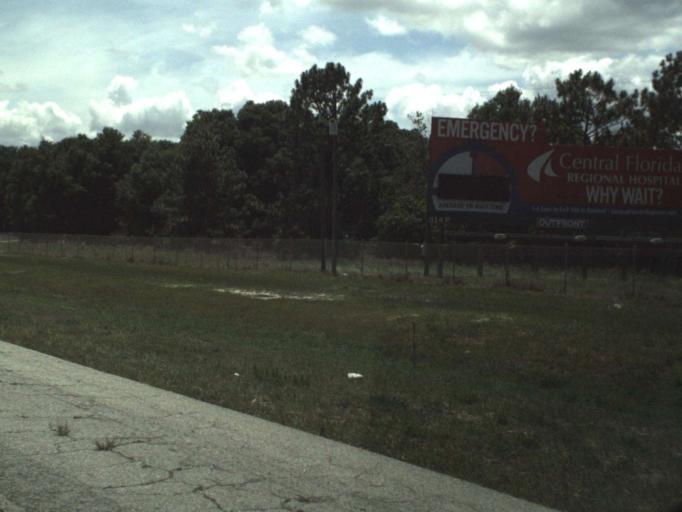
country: US
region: Florida
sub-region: Seminole County
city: Longwood
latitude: 28.7089
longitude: -81.3803
